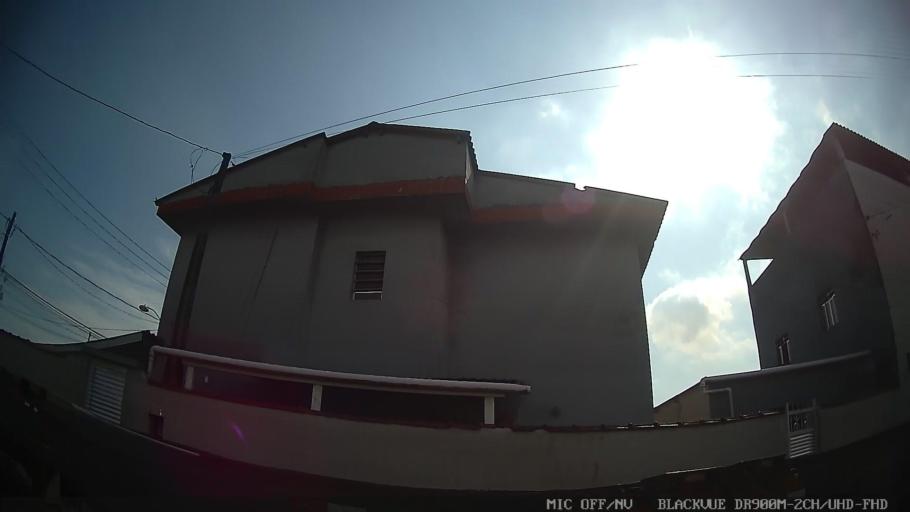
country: BR
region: Sao Paulo
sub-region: Santos
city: Santos
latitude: -23.9484
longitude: -46.3037
